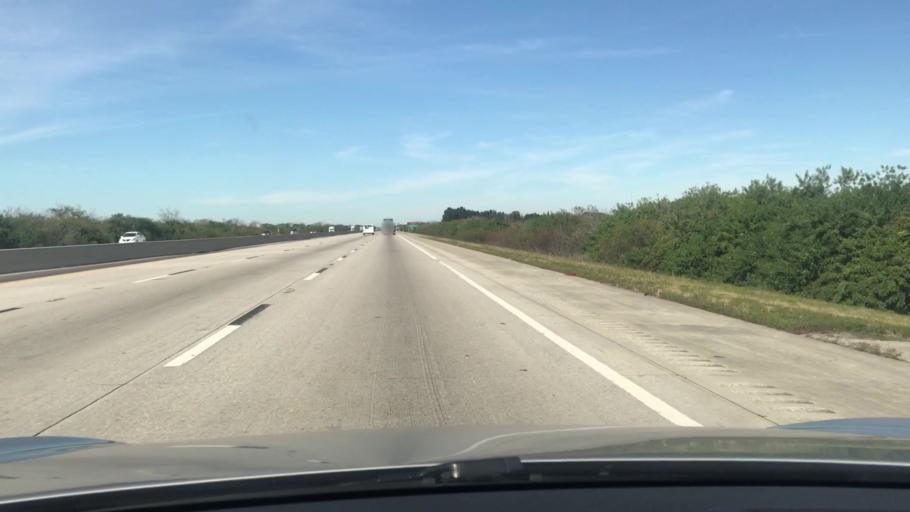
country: US
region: Florida
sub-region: Brevard County
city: Cocoa West
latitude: 28.3302
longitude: -80.7750
